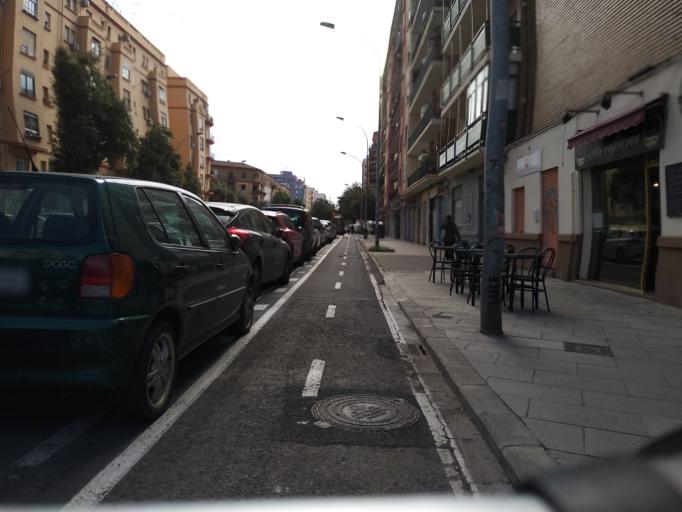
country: ES
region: Valencia
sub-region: Provincia de Valencia
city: Tavernes Blanques
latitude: 39.4850
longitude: -0.3703
